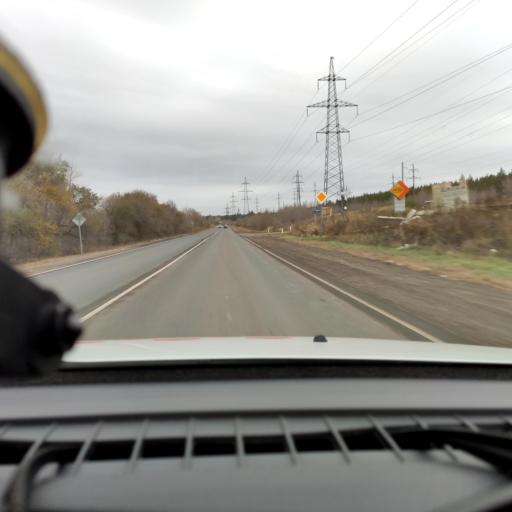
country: RU
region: Samara
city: Samara
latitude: 53.1182
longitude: 50.2191
